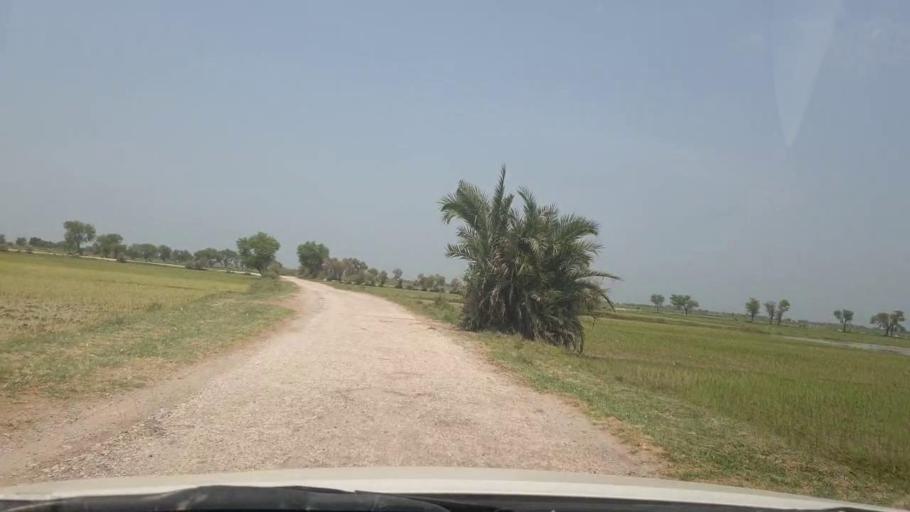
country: PK
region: Sindh
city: Rustam jo Goth
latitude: 28.0463
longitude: 68.7515
